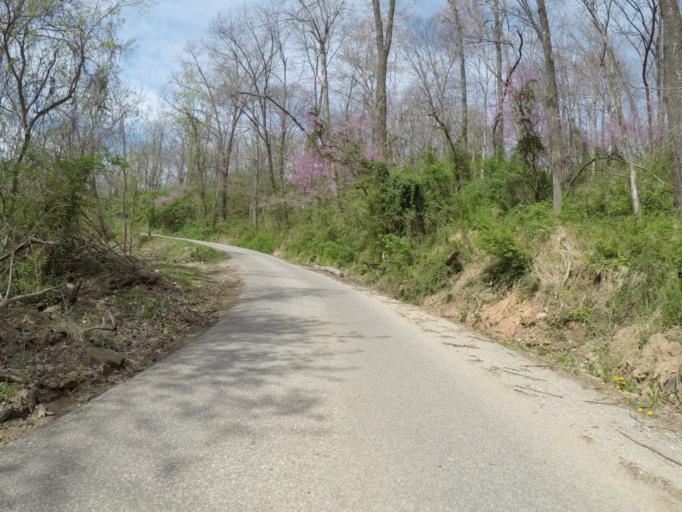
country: US
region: West Virginia
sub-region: Wayne County
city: Lavalette
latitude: 38.3445
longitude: -82.3668
